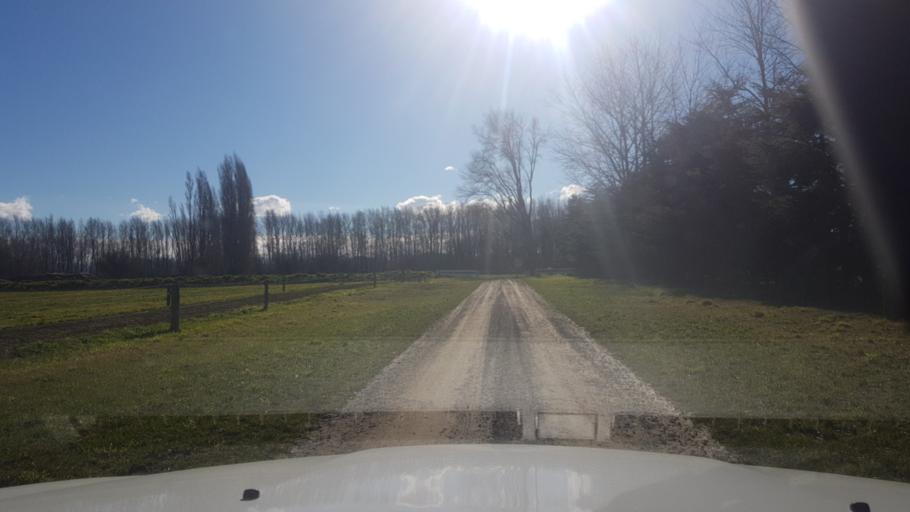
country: NZ
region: Canterbury
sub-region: Timaru District
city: Pleasant Point
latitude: -44.2512
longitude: 171.1092
